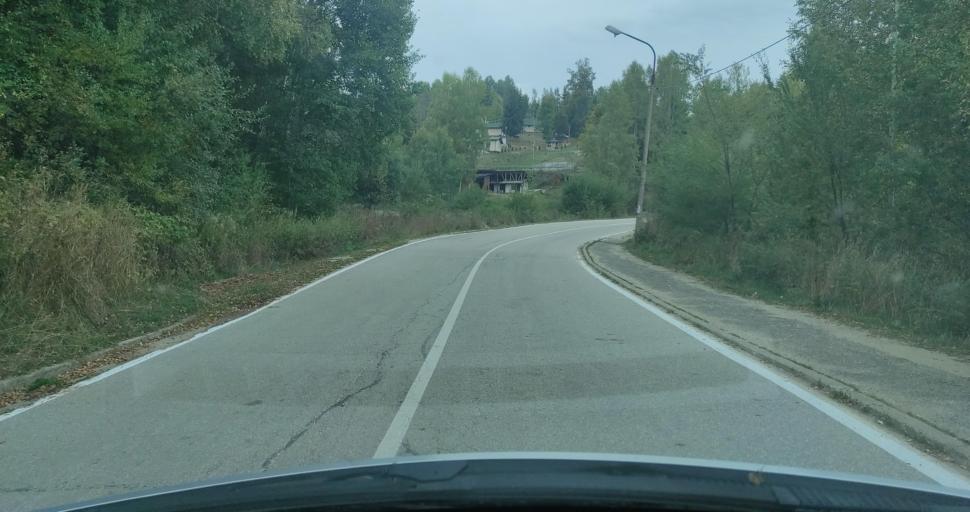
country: RS
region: Central Serbia
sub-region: Jablanicki Okrug
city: Crna Trava
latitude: 42.7398
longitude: 22.3294
